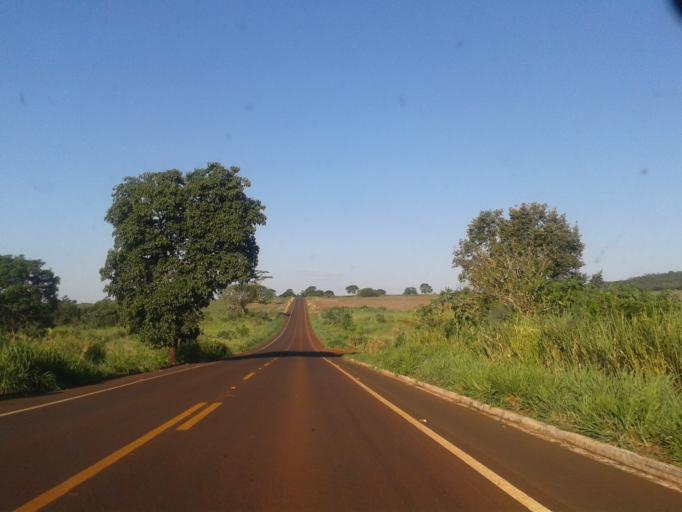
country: BR
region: Minas Gerais
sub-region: Capinopolis
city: Capinopolis
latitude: -18.7120
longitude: -49.8010
